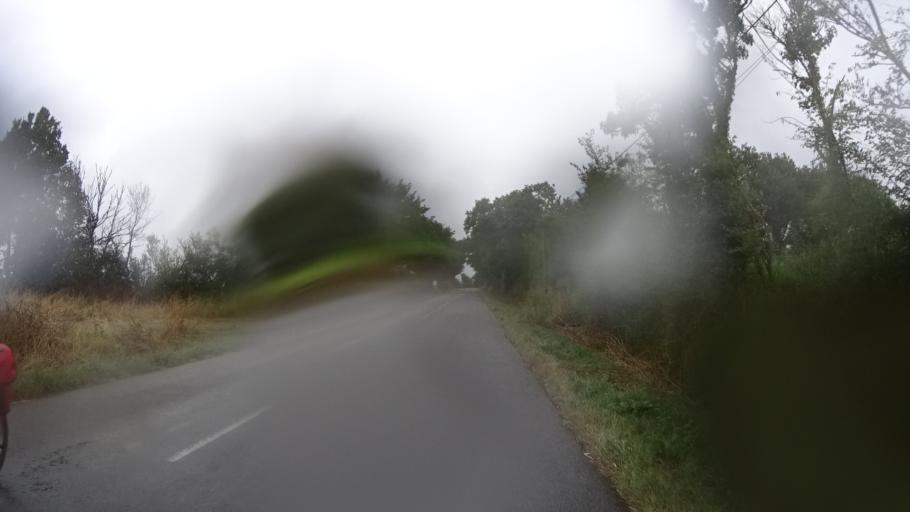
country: FR
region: Pays de la Loire
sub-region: Departement de la Loire-Atlantique
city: Corsept
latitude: 47.2682
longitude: -2.0913
